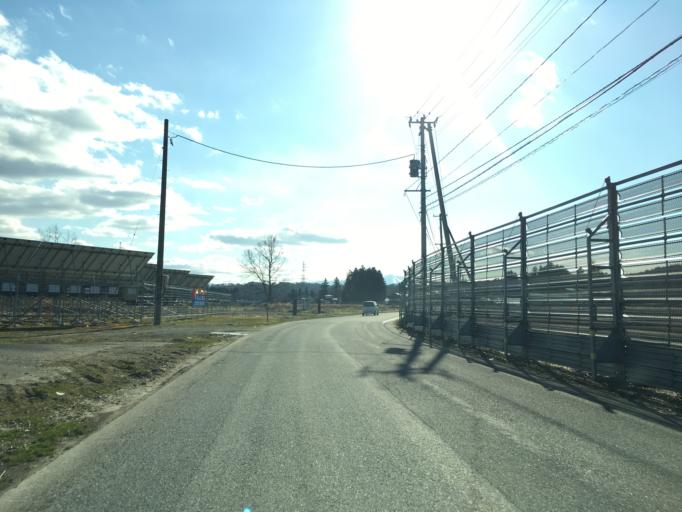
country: JP
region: Yamagata
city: Nagai
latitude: 38.0015
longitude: 140.0209
